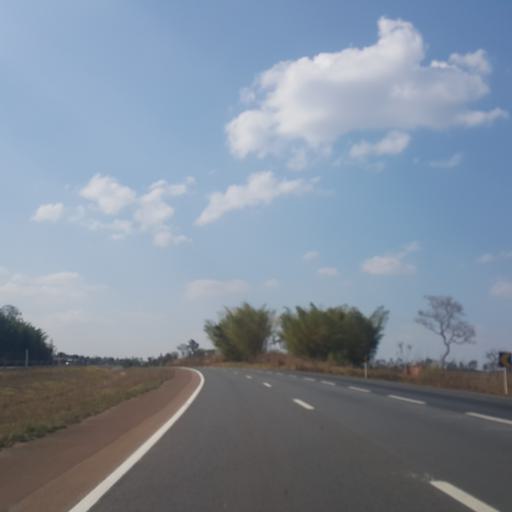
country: BR
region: Goias
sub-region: Abadiania
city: Abadiania
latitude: -16.2936
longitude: -48.8002
